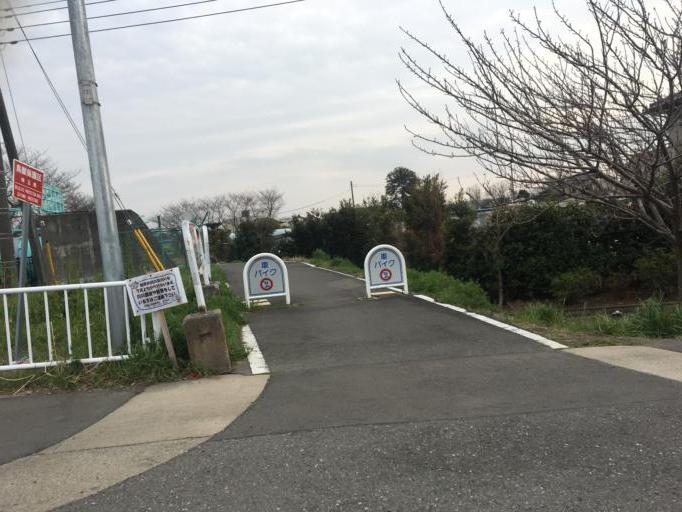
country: JP
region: Saitama
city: Oi
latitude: 35.8676
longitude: 139.5495
